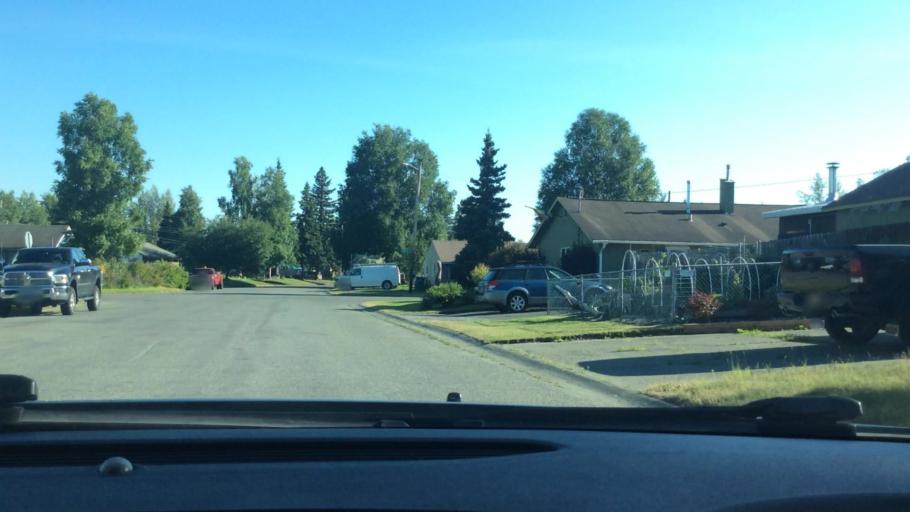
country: US
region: Alaska
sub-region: Anchorage Municipality
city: Anchorage
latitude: 61.2080
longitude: -149.7701
